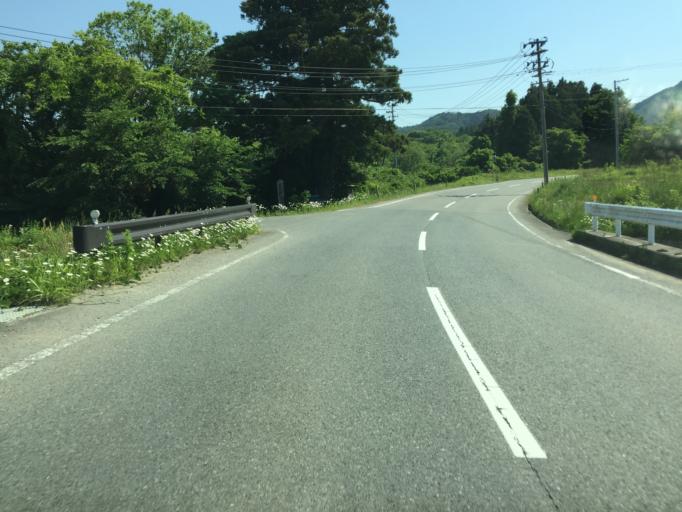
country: JP
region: Miyagi
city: Marumori
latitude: 37.8136
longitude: 140.8833
